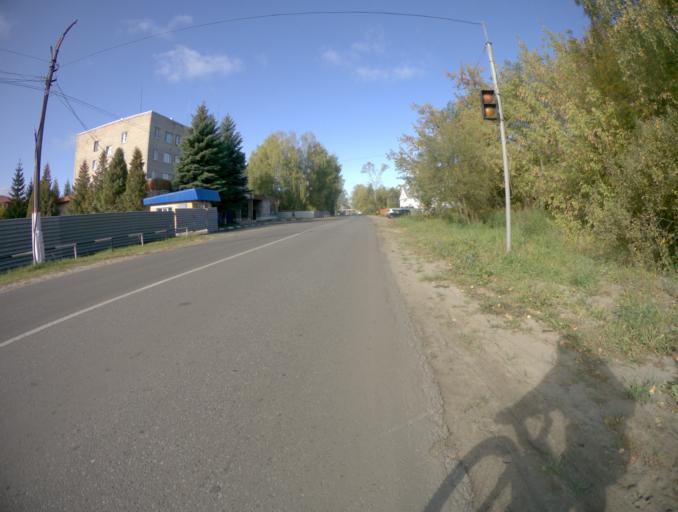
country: RU
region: Moskovskaya
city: Roshal'
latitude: 55.6600
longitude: 39.8830
